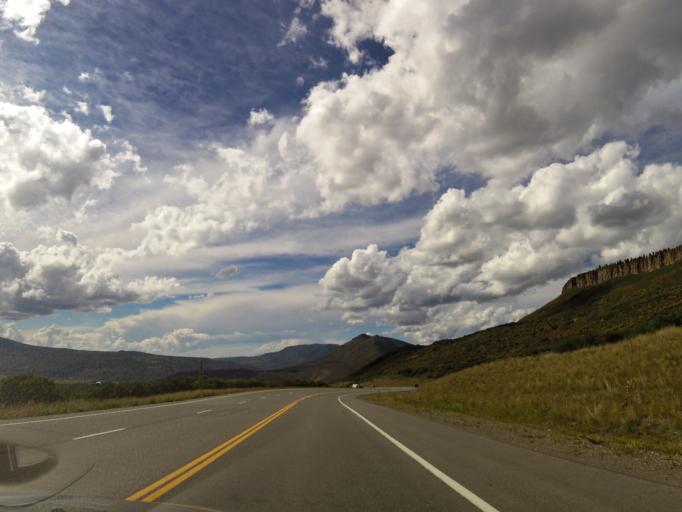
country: US
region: Colorado
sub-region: Hinsdale County
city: Lake City
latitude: 38.3938
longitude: -107.4458
